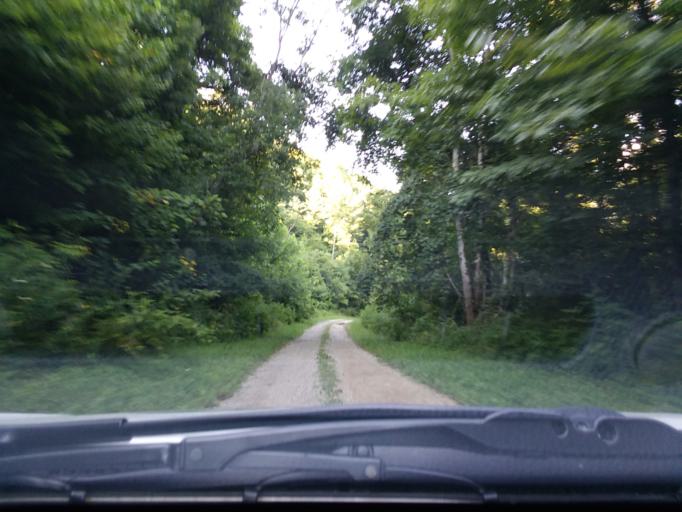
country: US
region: Tennessee
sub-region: Clay County
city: Celina
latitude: 36.6340
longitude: -85.4188
